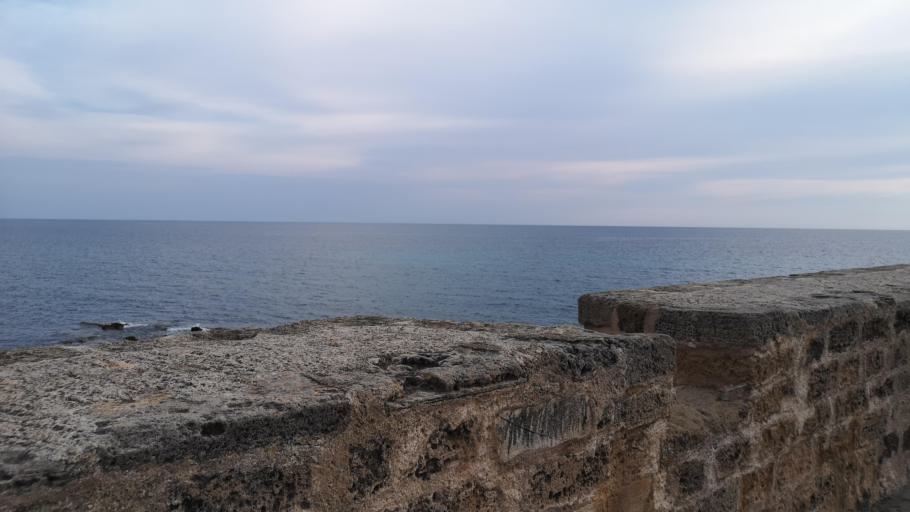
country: IT
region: Sardinia
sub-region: Provincia di Sassari
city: Alghero
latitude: 40.5591
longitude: 8.3113
